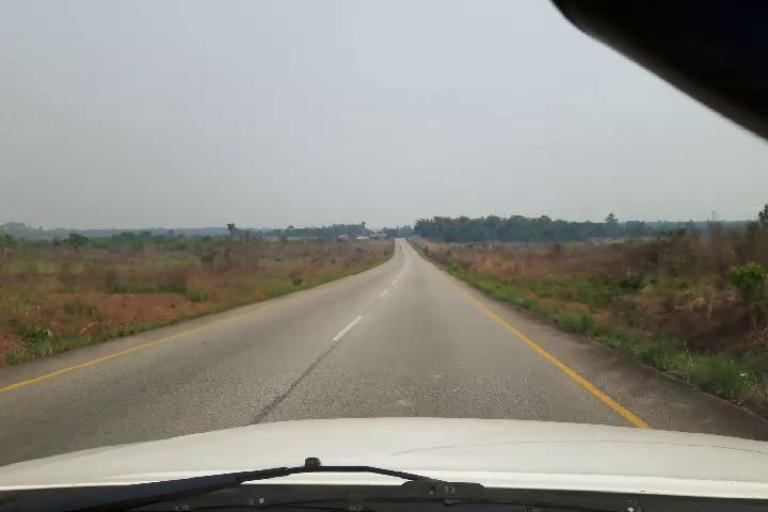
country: SL
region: Southern Province
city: Largo
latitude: 8.2250
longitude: -12.0760
